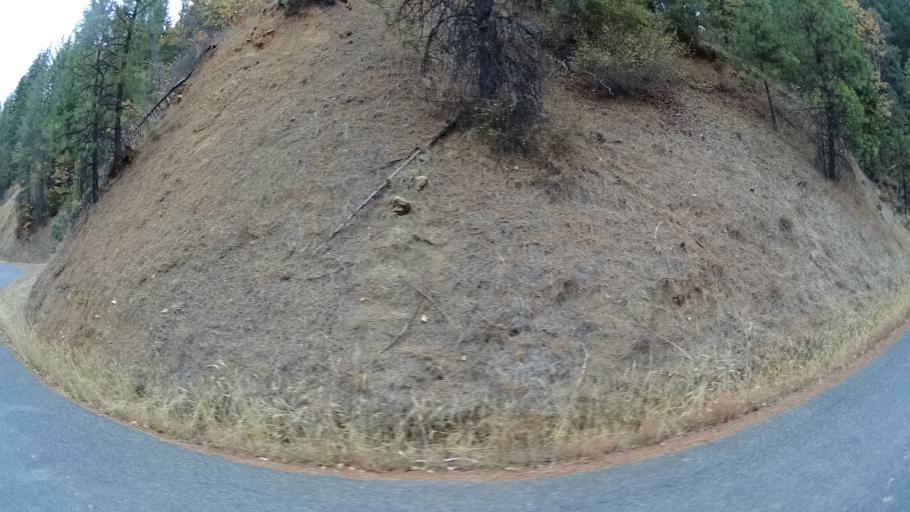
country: US
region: California
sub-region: Siskiyou County
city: Happy Camp
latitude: 41.7726
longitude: -123.3751
